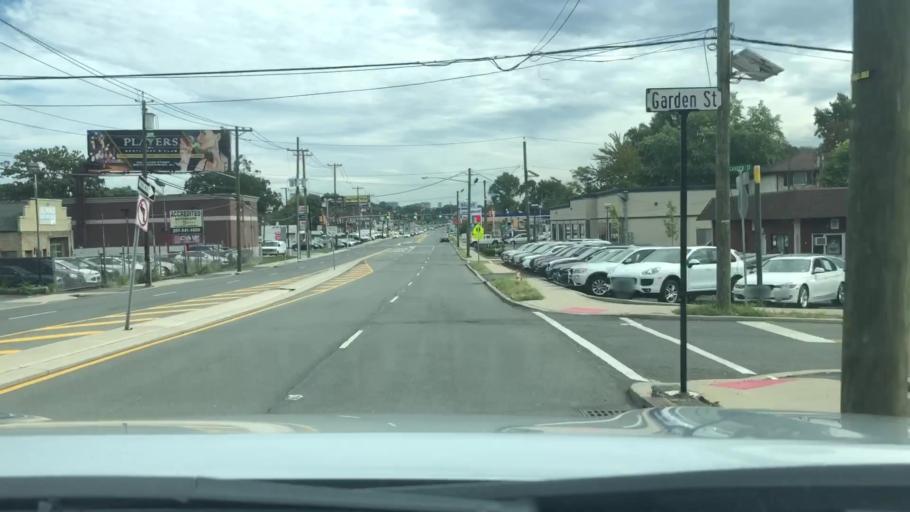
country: US
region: New Jersey
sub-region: Bergen County
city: Little Ferry
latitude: 40.8542
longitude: -74.0401
